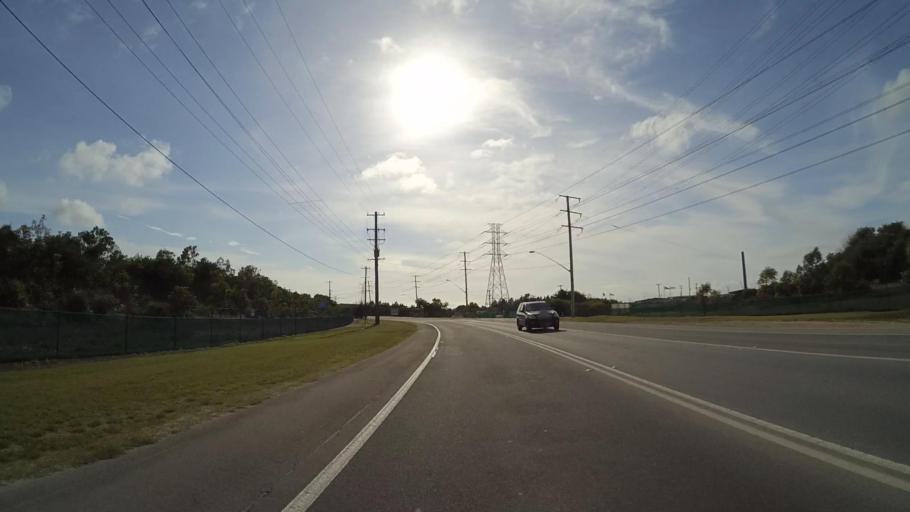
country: AU
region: New South Wales
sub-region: Sutherland Shire
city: Kurnell
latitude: -34.0246
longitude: 151.1880
